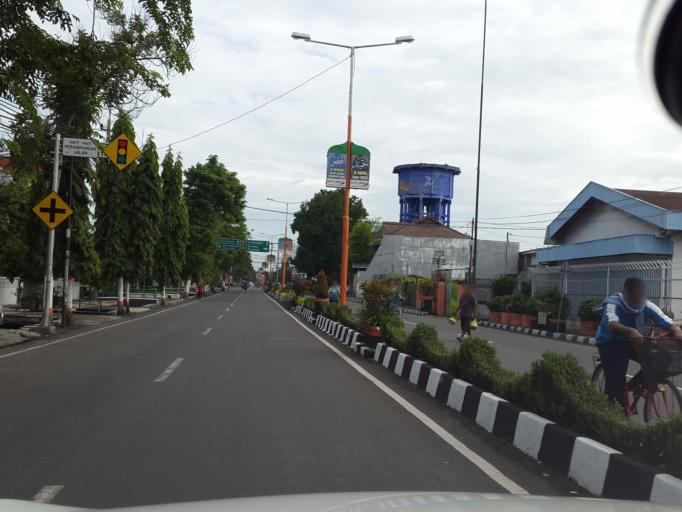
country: ID
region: East Java
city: Mojokerto
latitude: -7.4682
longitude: 112.4395
